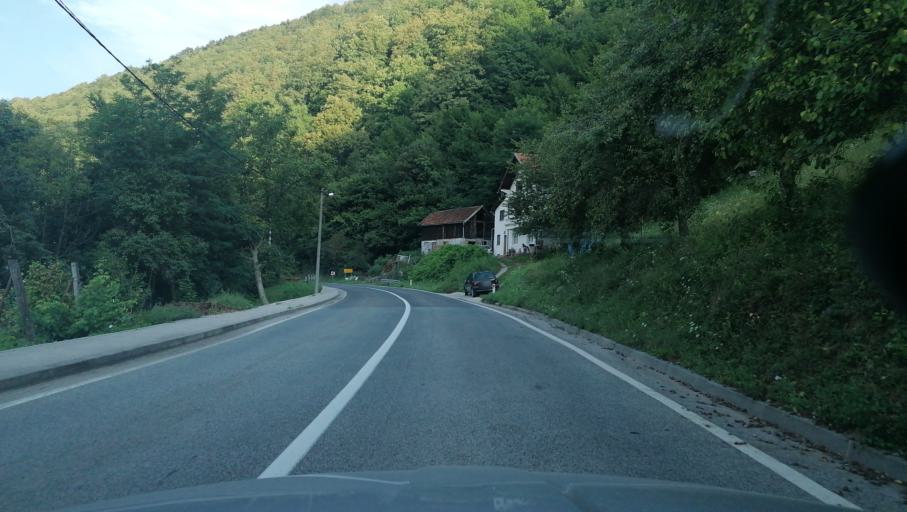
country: BA
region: Federation of Bosnia and Herzegovina
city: Jajce
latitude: 44.2326
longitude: 17.3138
